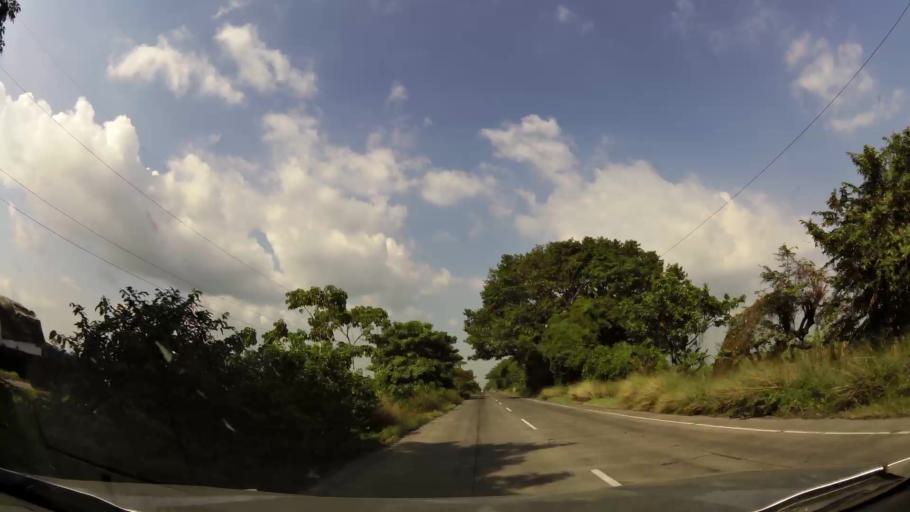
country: GT
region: Escuintla
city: Puerto San Jose
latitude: 14.0178
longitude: -90.7836
